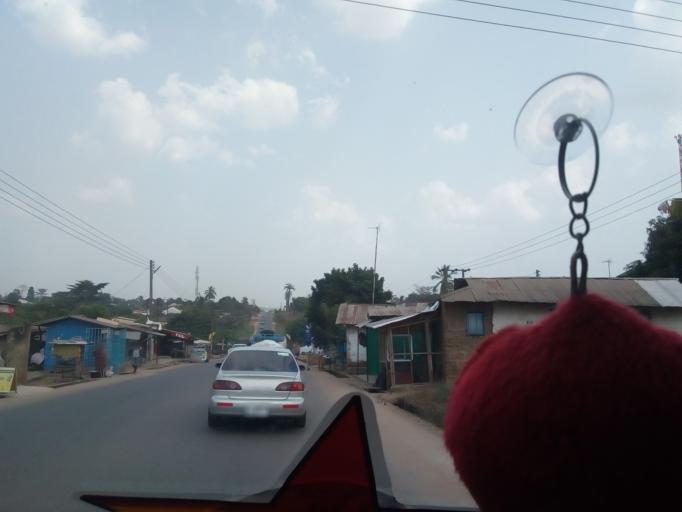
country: GH
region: Eastern
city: Suhum
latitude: 6.0414
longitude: -0.4434
